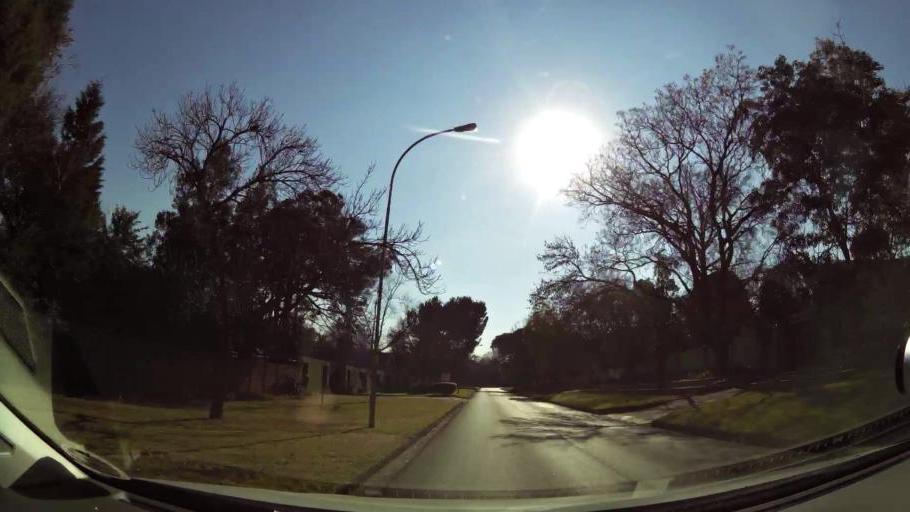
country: ZA
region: Gauteng
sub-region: City of Johannesburg Metropolitan Municipality
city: Modderfontein
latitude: -26.1604
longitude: 28.1355
